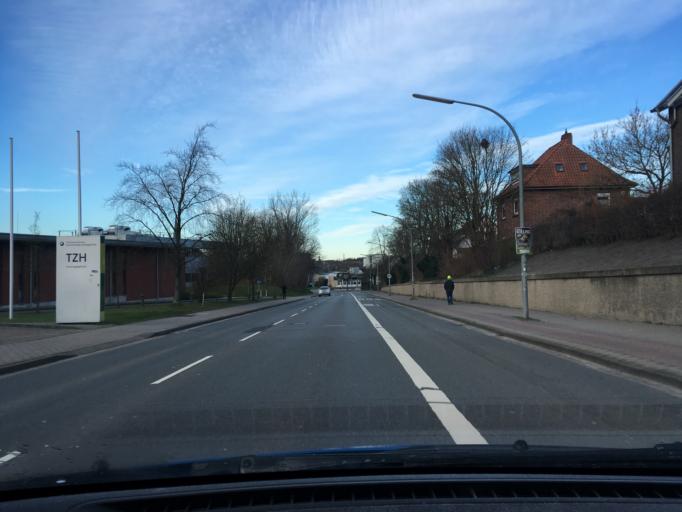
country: DE
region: Lower Saxony
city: Lueneburg
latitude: 53.2484
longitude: 10.4270
